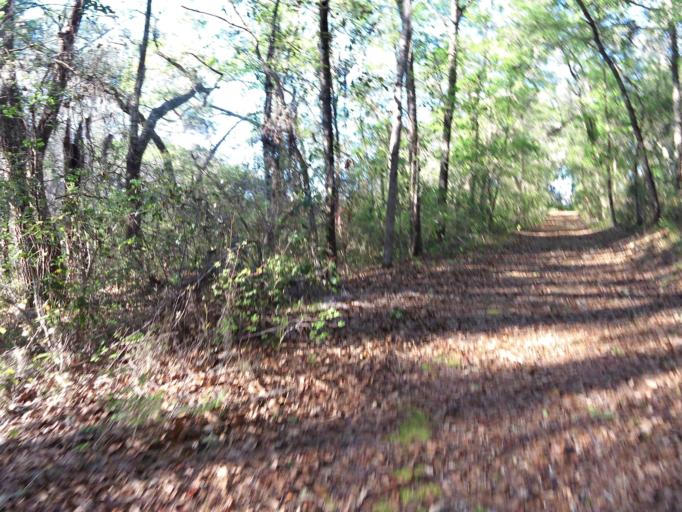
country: US
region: Florida
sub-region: Clay County
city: Keystone Heights
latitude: 29.8186
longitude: -82.0195
